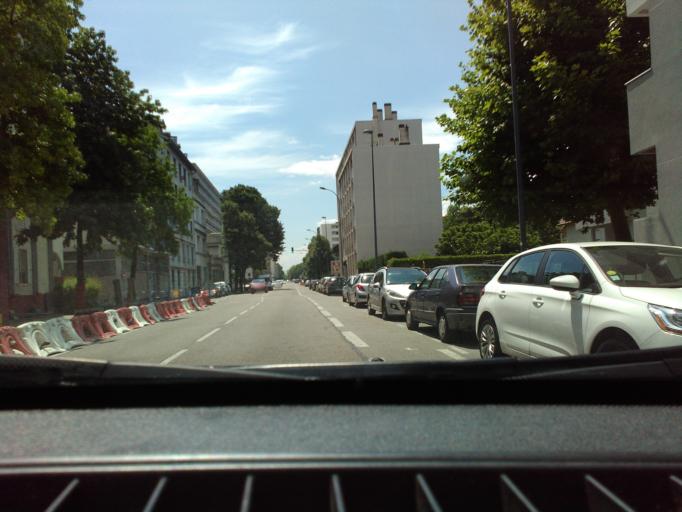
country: FR
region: Rhone-Alpes
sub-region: Departement de l'Isere
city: Seyssinet-Pariset
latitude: 45.1830
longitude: 5.7055
